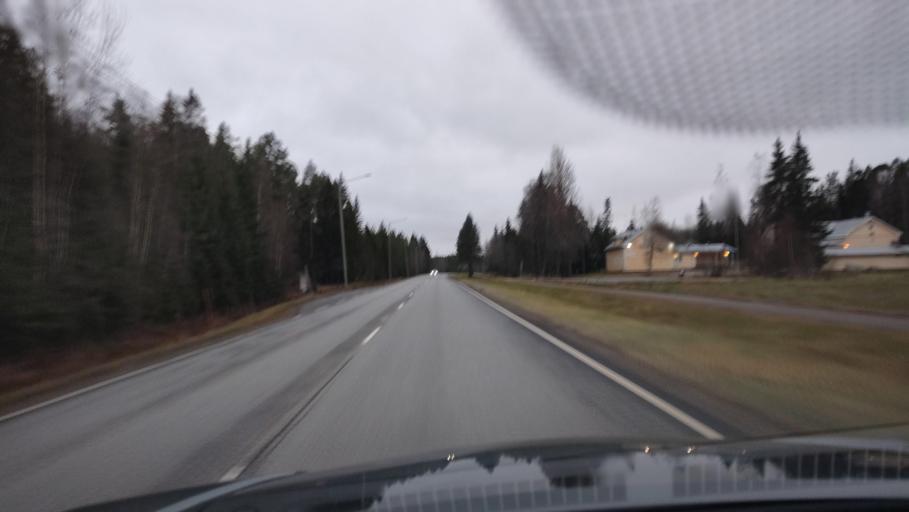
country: FI
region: Southern Ostrobothnia
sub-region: Suupohja
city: Kauhajoki
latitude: 62.3990
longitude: 22.1582
